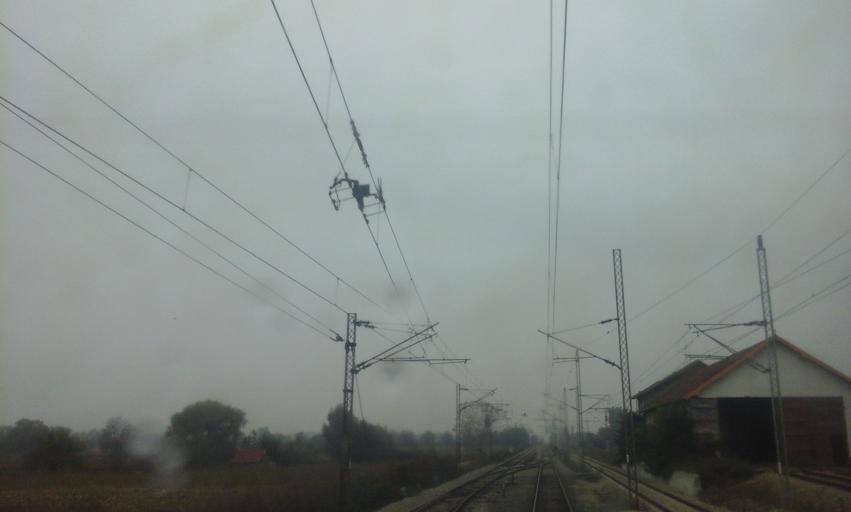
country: RS
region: Central Serbia
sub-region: Pomoravski Okrug
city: Paracin
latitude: 43.8701
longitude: 21.3950
